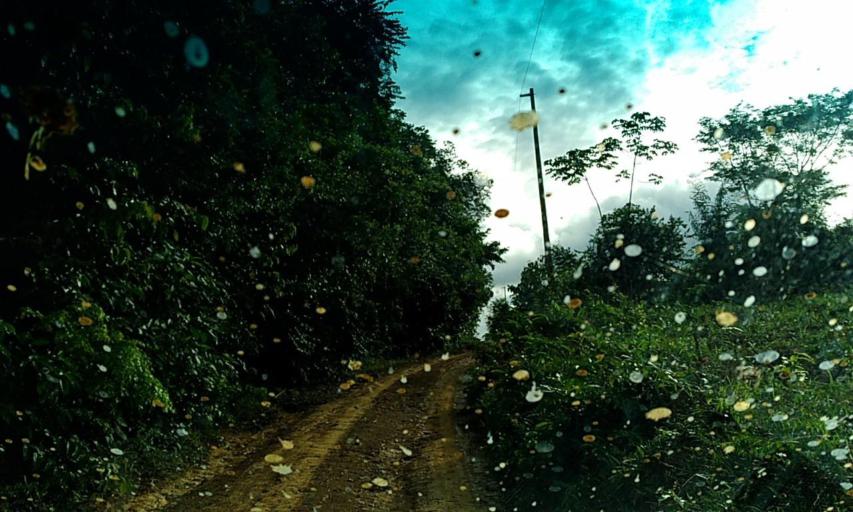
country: BR
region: Para
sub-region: Senador Jose Porfirio
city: Senador Jose Porfirio
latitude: -3.0078
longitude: -51.7456
